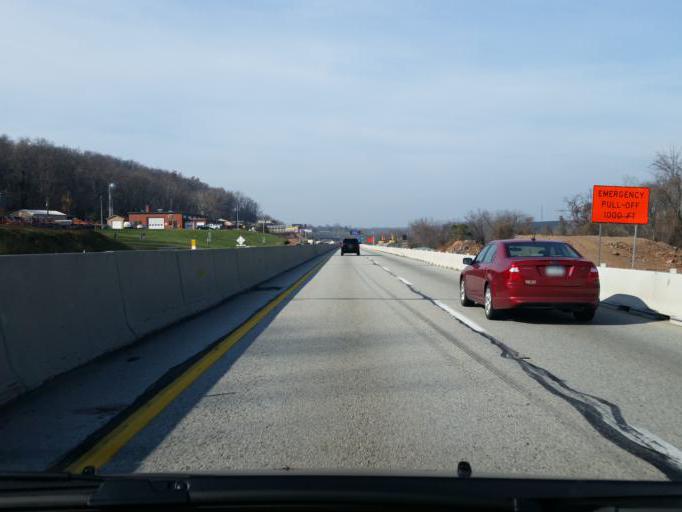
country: US
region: Pennsylvania
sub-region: Dauphin County
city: Enhaut
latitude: 40.2003
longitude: -76.8397
